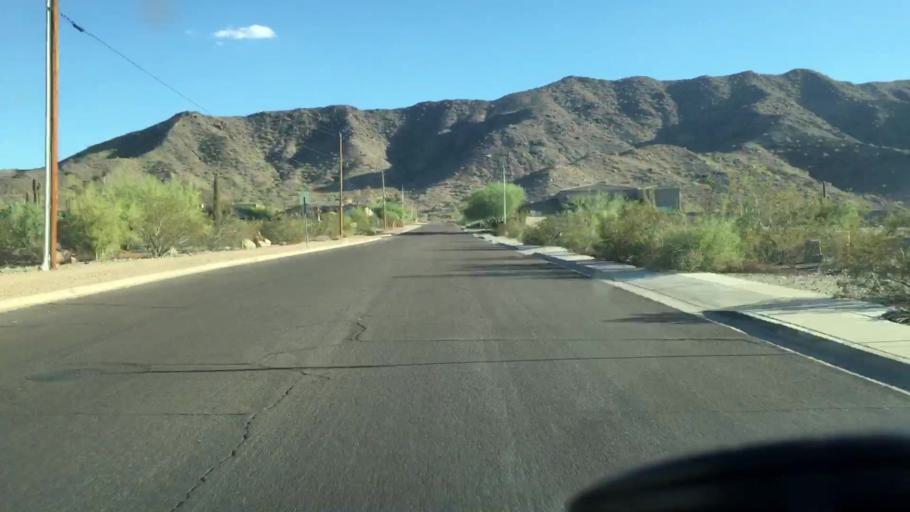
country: US
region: Arizona
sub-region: Maricopa County
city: Laveen
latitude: 33.3604
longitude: -112.0987
